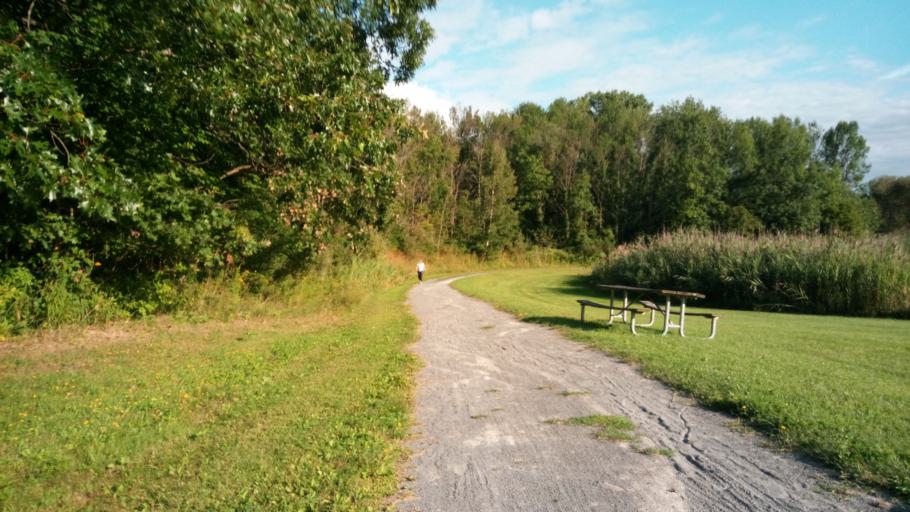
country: US
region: New York
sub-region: Ontario County
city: Victor
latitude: 42.9978
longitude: -77.4399
